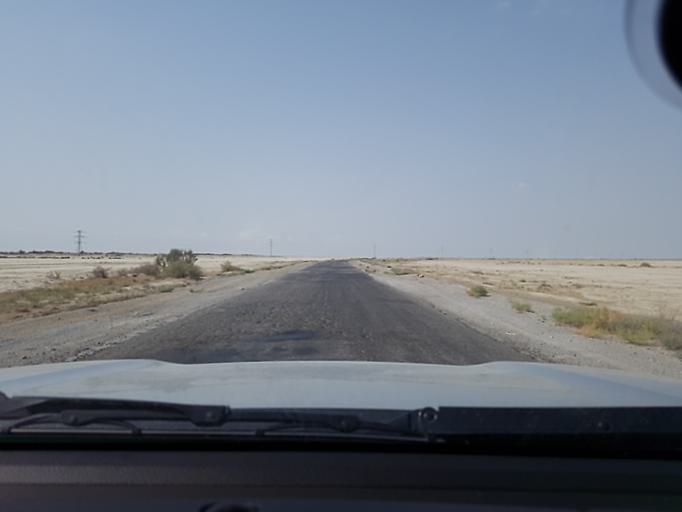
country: TM
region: Balkan
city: Gumdag
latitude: 38.7676
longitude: 54.5856
